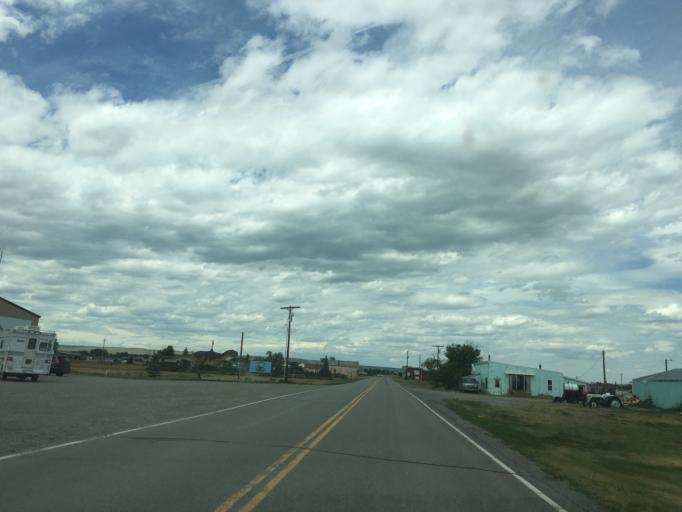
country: US
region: Montana
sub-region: Teton County
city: Choteau
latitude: 47.9757
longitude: -112.3107
